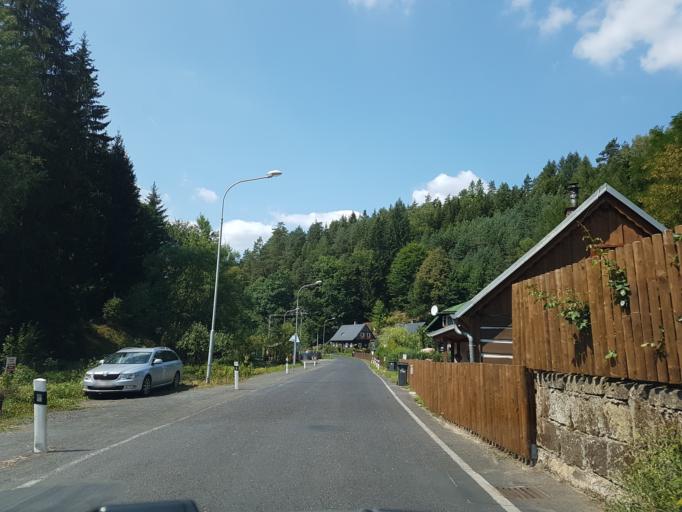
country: CZ
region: Ustecky
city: Ceska Kamenice
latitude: 50.8529
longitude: 14.3796
